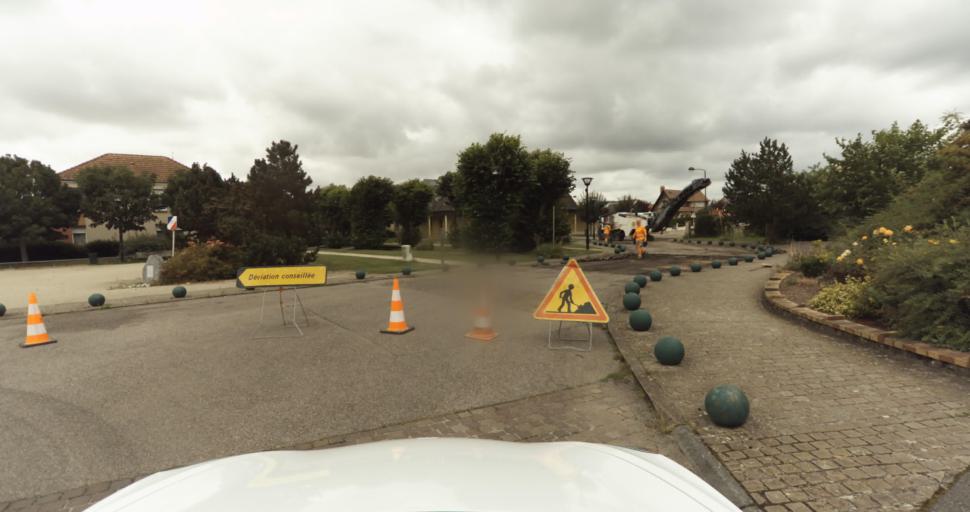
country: FR
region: Haute-Normandie
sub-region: Departement de l'Eure
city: Saint-Sebastien-de-Morsent
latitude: 49.0095
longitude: 1.0879
